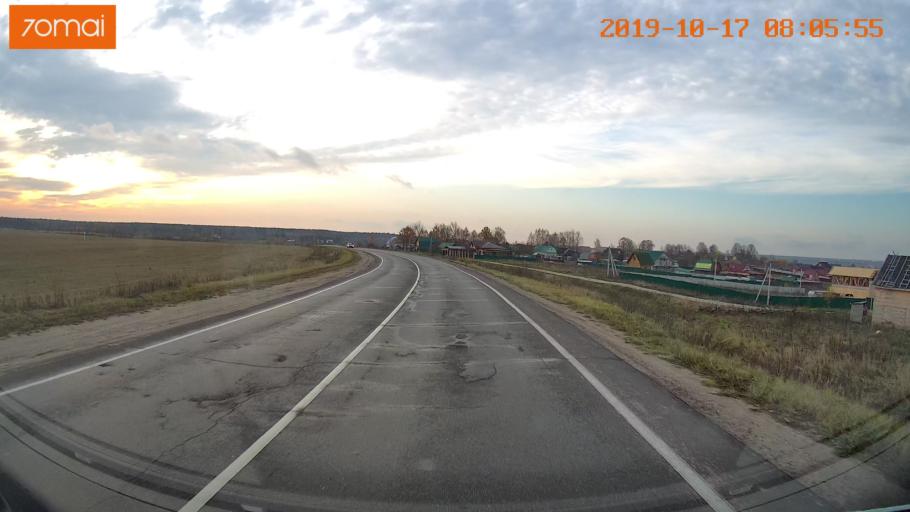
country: RU
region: Vladimir
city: Kol'chugino
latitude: 56.3290
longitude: 39.4104
